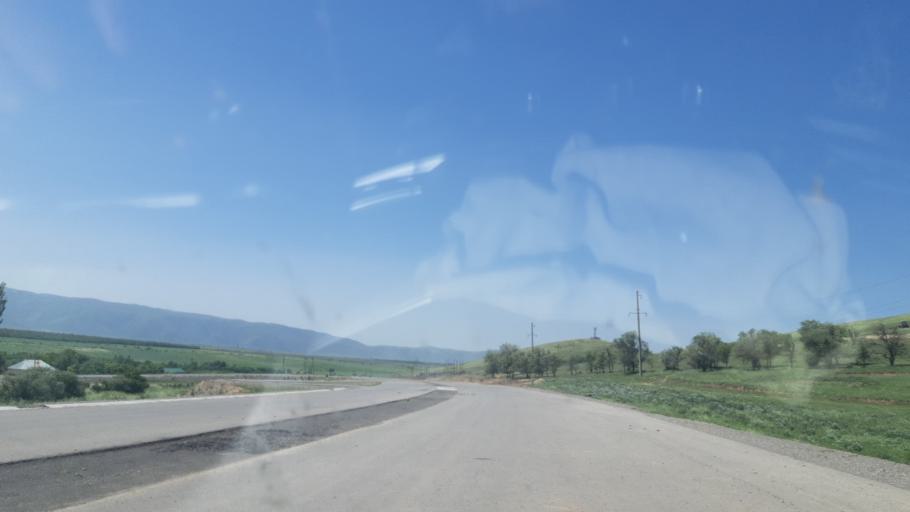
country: KZ
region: Ongtustik Qazaqstan
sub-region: Tulkibas Audany
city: Zhabagly
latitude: 42.5171
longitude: 70.5348
